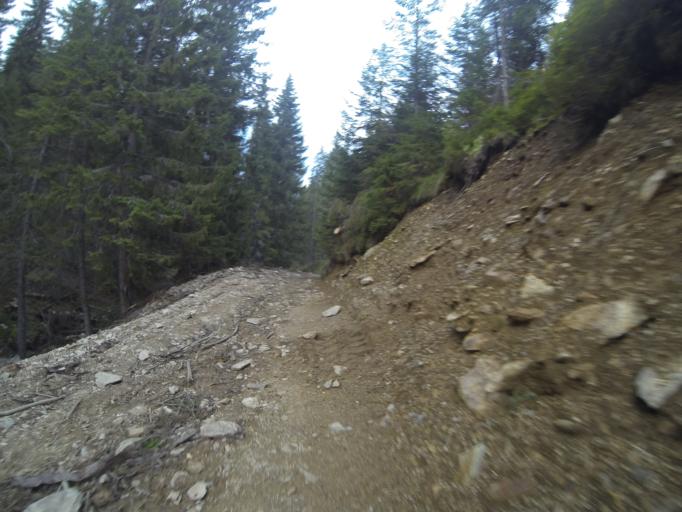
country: RO
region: Gorj
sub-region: Comuna Polovragi
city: Polovragi
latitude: 45.2978
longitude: 23.8388
